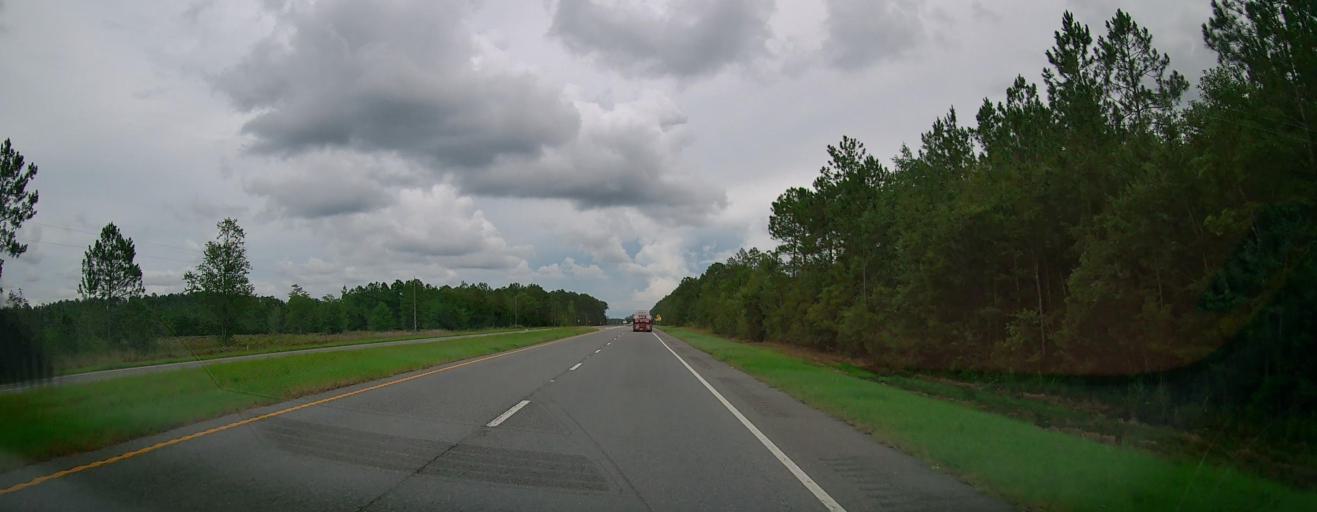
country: US
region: Georgia
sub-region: Wayne County
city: Jesup
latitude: 31.6726
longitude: -82.0636
